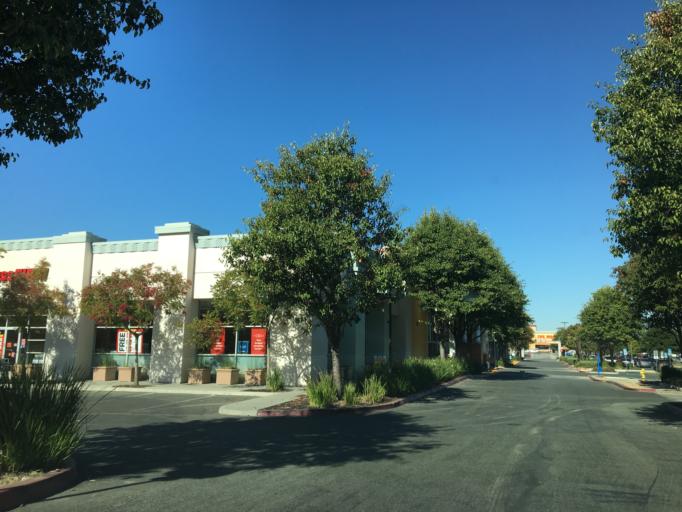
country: US
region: California
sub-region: Santa Clara County
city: Seven Trees
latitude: 37.3009
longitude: -121.8657
